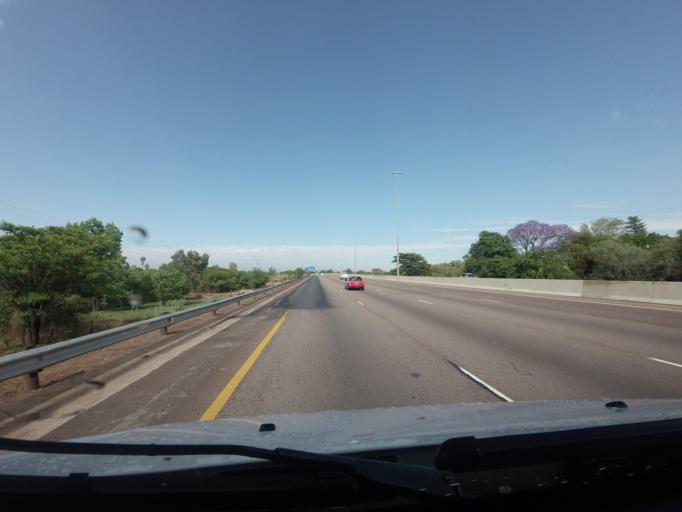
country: ZA
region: Gauteng
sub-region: City of Tshwane Metropolitan Municipality
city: Pretoria
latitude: -25.7021
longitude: 28.2737
